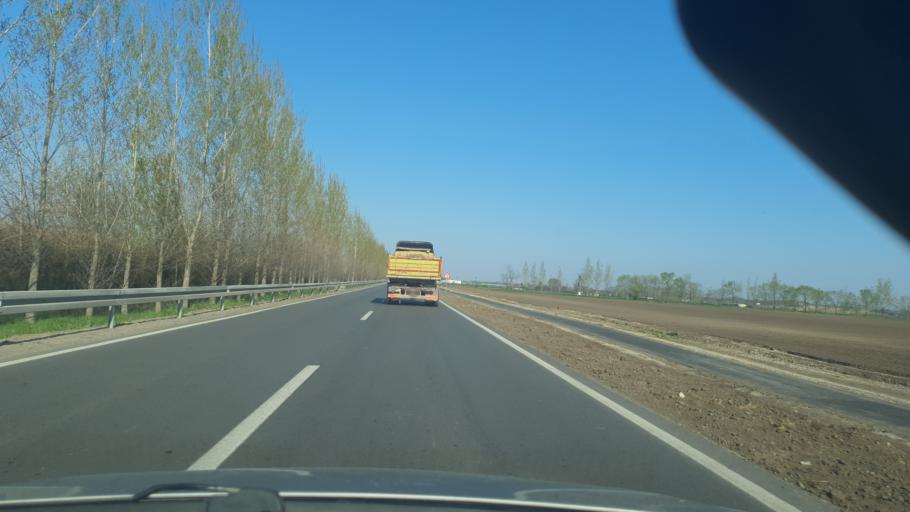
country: RS
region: Autonomna Pokrajina Vojvodina
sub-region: Juznobacki Okrug
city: Vrbas
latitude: 45.5923
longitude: 19.5883
